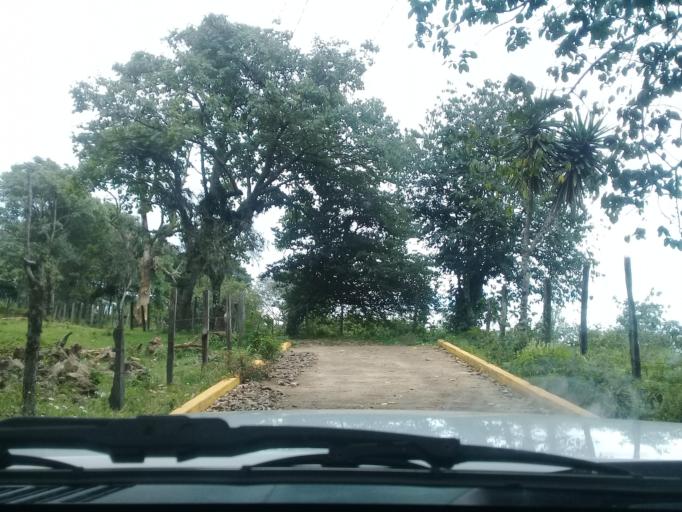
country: MX
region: Veracruz
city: Rafael Lucio
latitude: 19.6030
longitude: -96.9894
